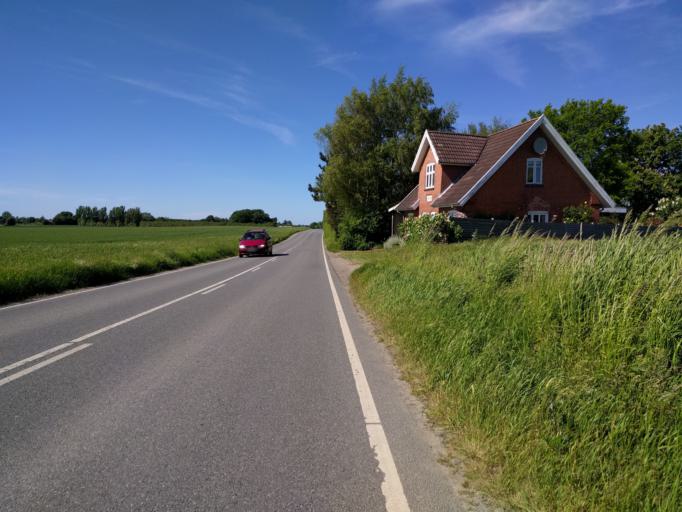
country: DK
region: South Denmark
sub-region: Kerteminde Kommune
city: Langeskov
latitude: 55.3896
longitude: 10.6076
